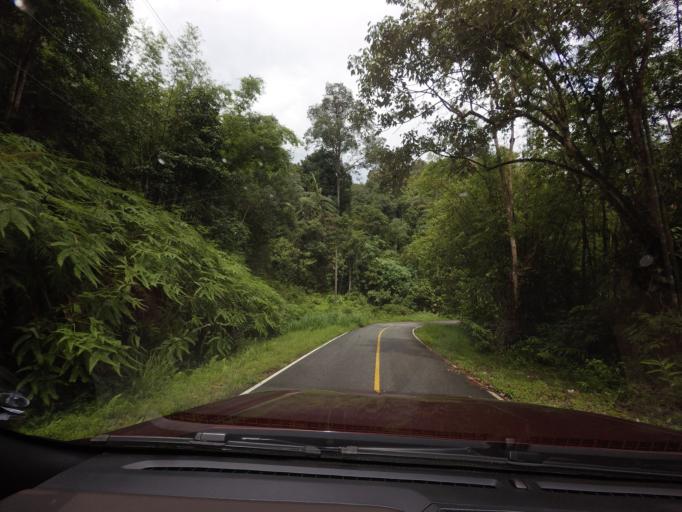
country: TH
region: Narathiwat
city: Sukhirin
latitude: 5.9439
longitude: 101.6525
